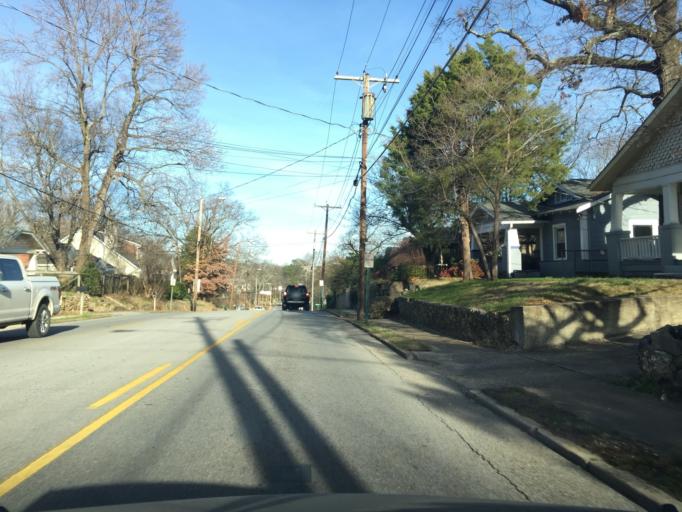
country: US
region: Tennessee
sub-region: Hamilton County
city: Chattanooga
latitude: 35.0652
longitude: -85.2945
